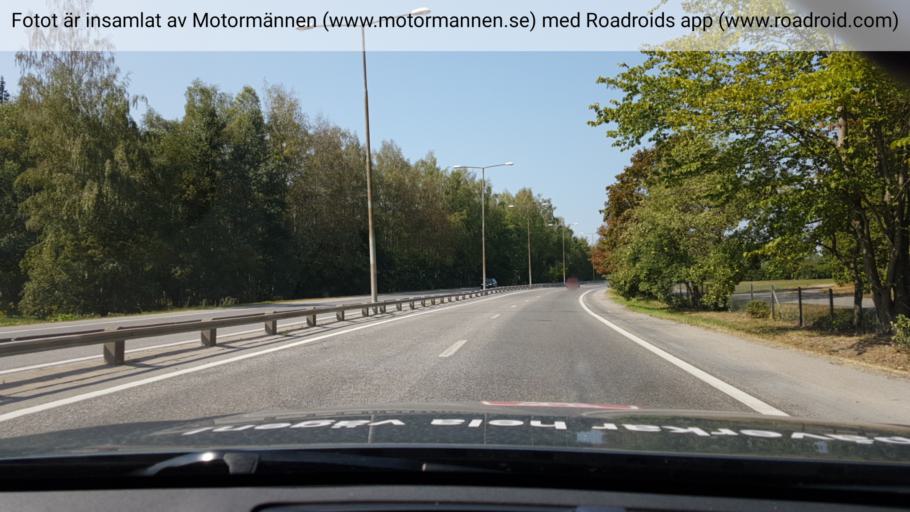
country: SE
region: Stockholm
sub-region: Stockholms Kommun
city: Arsta
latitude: 59.2631
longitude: 18.0279
